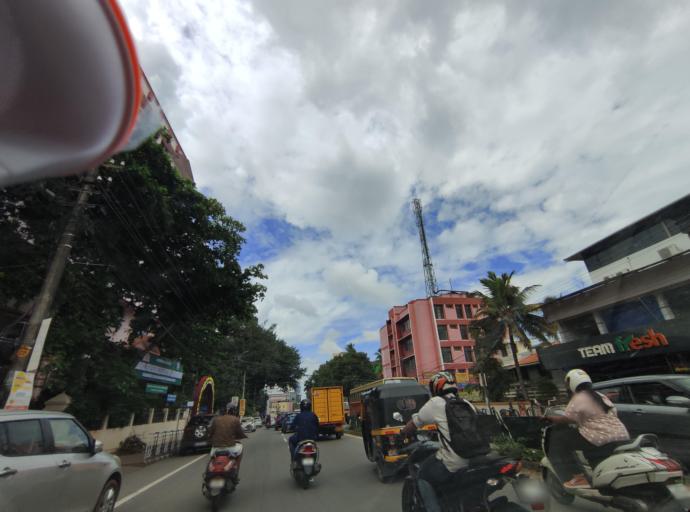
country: IN
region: Kerala
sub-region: Thiruvananthapuram
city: Thiruvananthapuram
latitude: 8.5218
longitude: 76.9413
